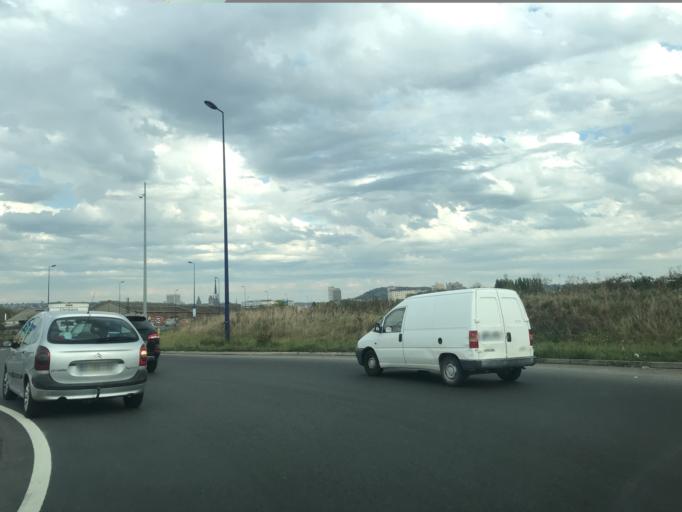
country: FR
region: Haute-Normandie
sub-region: Departement de la Seine-Maritime
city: Le Petit-Quevilly
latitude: 49.4372
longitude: 1.0668
